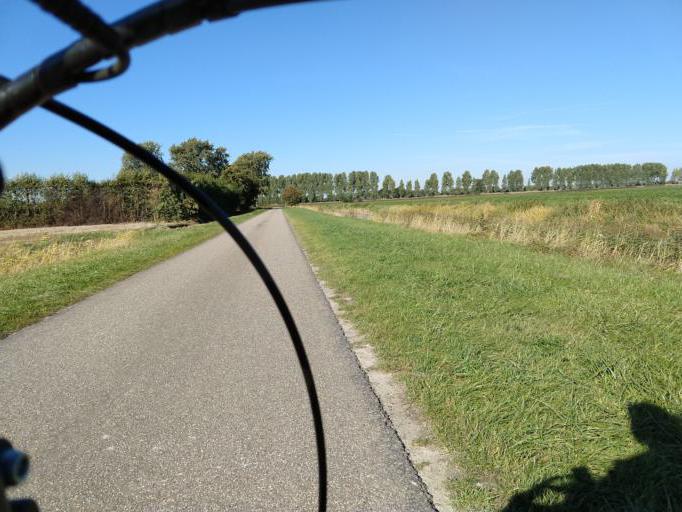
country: NL
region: Zeeland
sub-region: Gemeente Terneuzen
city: Terneuzen
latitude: 51.4007
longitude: 3.8265
